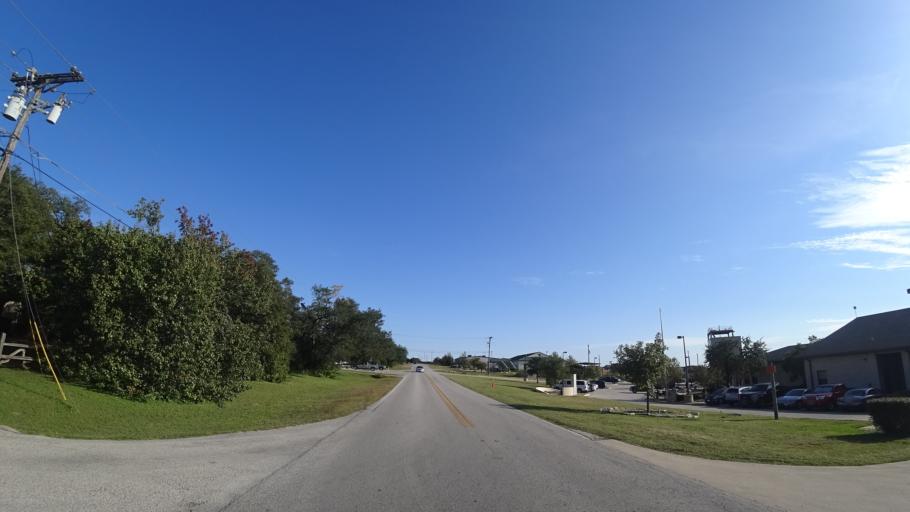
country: US
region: Texas
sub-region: Travis County
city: Barton Creek
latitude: 30.2398
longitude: -97.9195
